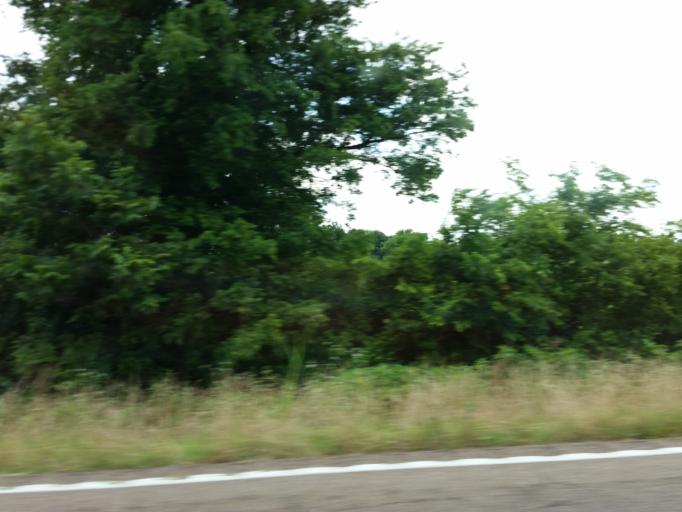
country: US
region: Tennessee
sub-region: Lake County
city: Tiptonville
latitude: 36.4002
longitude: -89.4544
